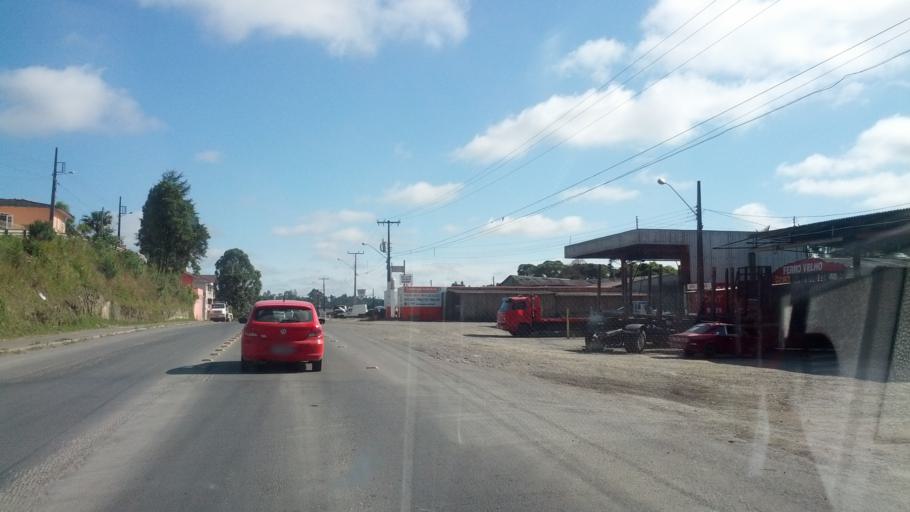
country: BR
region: Santa Catarina
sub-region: Otacilio Costa
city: Otacilio Costa
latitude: -27.4978
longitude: -50.1225
